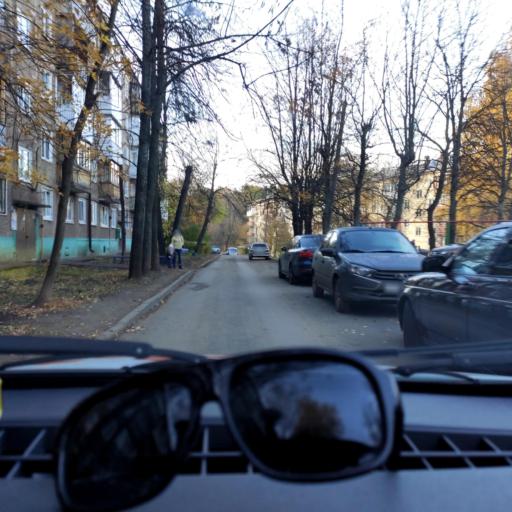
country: RU
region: Bashkortostan
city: Ufa
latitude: 54.7614
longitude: 55.9930
